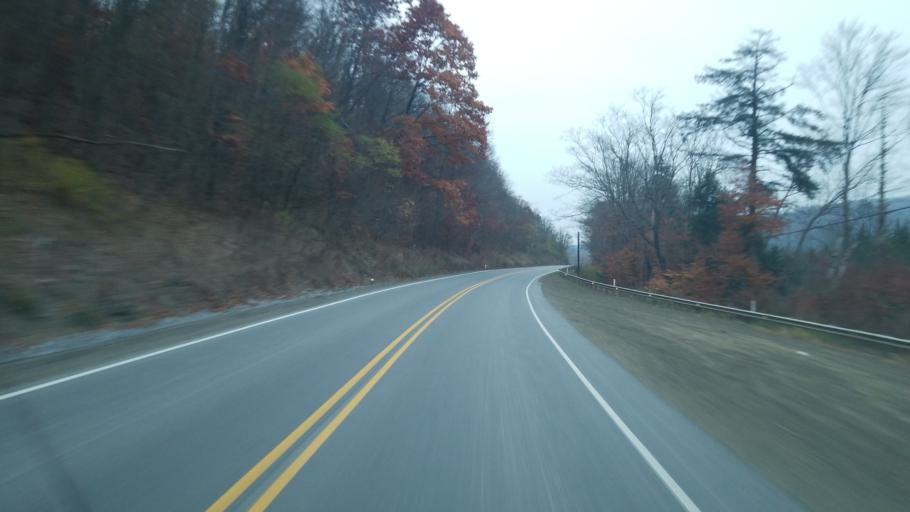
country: US
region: Pennsylvania
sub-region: McKean County
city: Smethport
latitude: 41.7901
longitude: -78.4153
